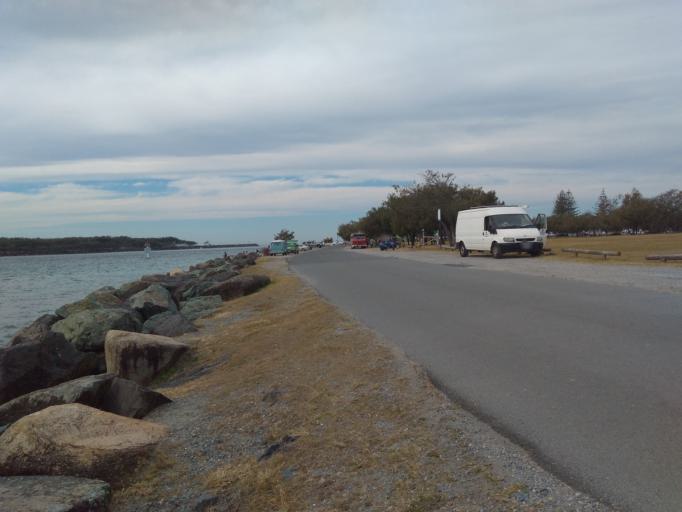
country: AU
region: Queensland
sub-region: Gold Coast
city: Southport
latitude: -27.9381
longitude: 153.4233
